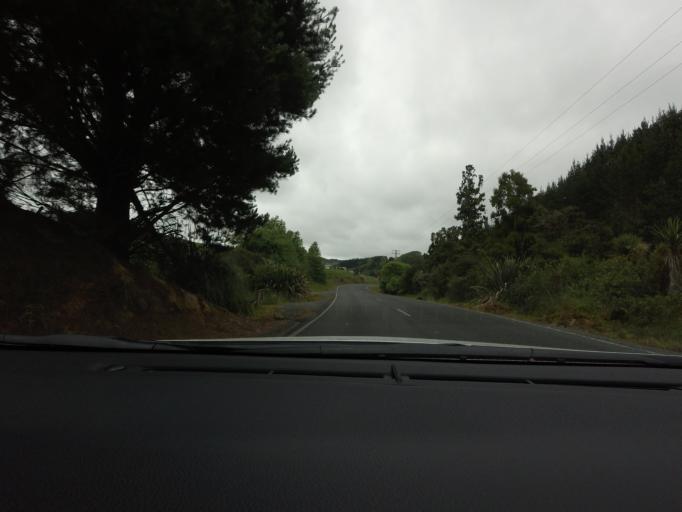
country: NZ
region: Auckland
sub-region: Auckland
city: Warkworth
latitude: -36.4681
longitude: 174.5469
